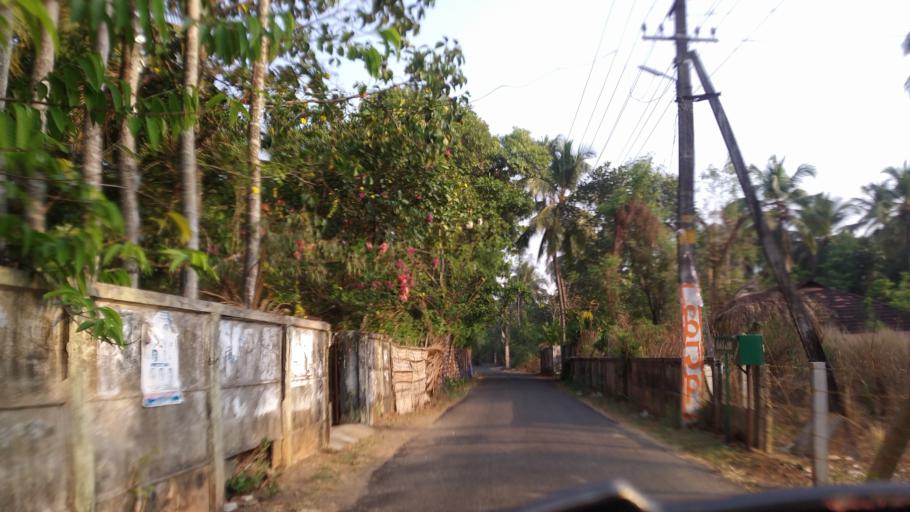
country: IN
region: Kerala
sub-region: Thrissur District
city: Thanniyam
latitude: 10.4290
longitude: 76.0802
